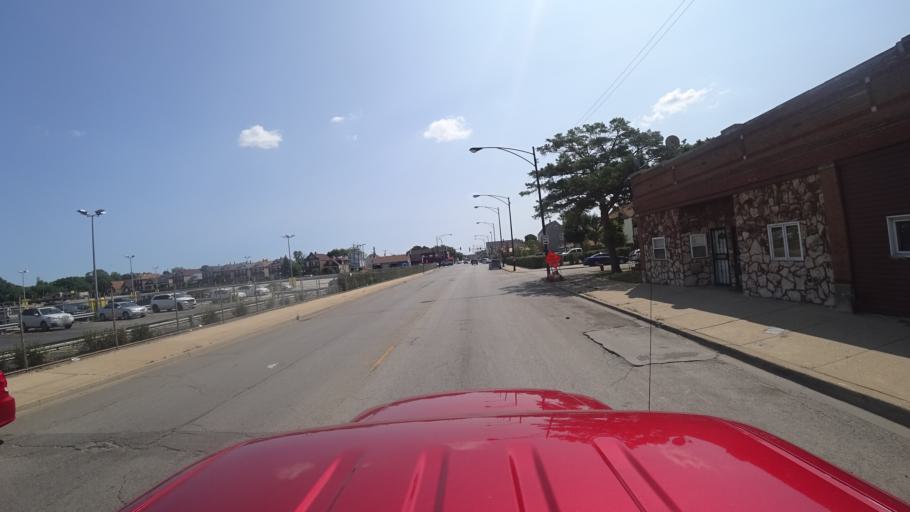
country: US
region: Illinois
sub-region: Cook County
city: Chicago
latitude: 41.8010
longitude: -87.6957
